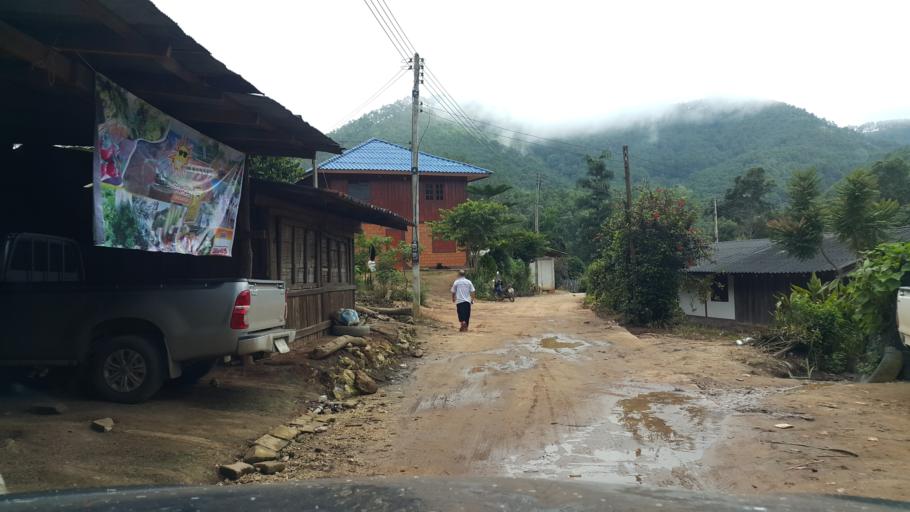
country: TH
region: Chiang Mai
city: Samoeng
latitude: 18.8802
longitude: 98.5134
